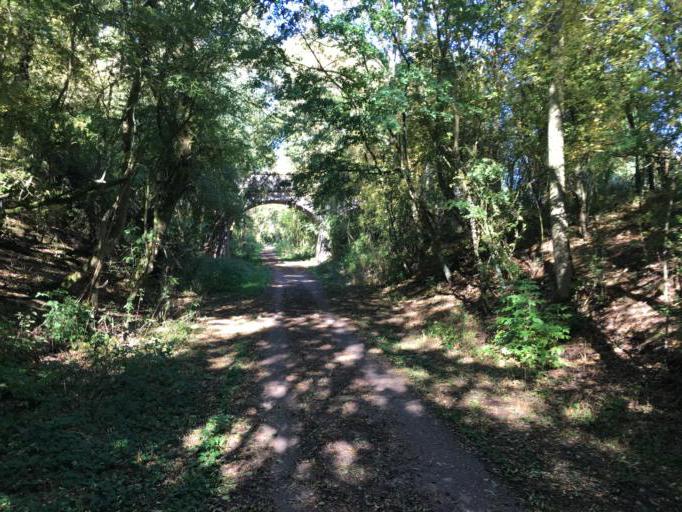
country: GB
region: England
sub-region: Warwickshire
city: Kenilworth
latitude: 52.3767
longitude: -1.6010
